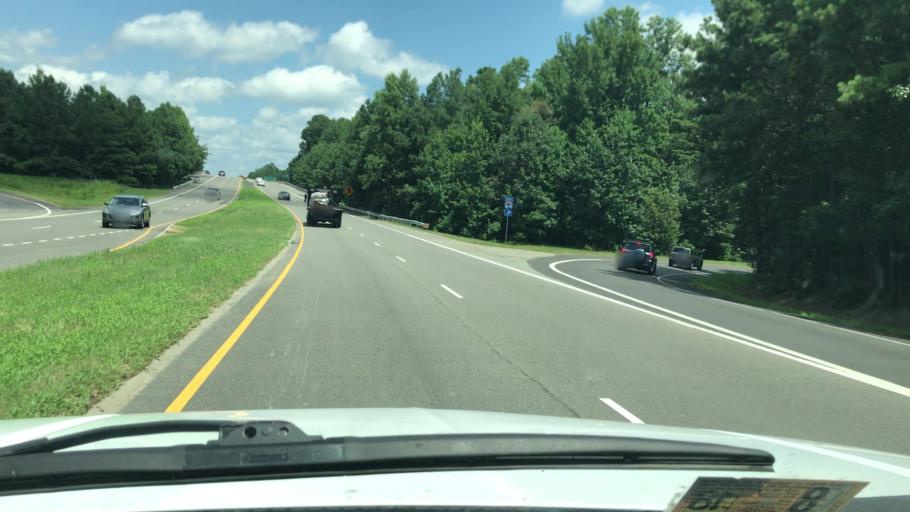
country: US
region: Virginia
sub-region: Henrico County
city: Short Pump
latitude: 37.6318
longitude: -77.5766
